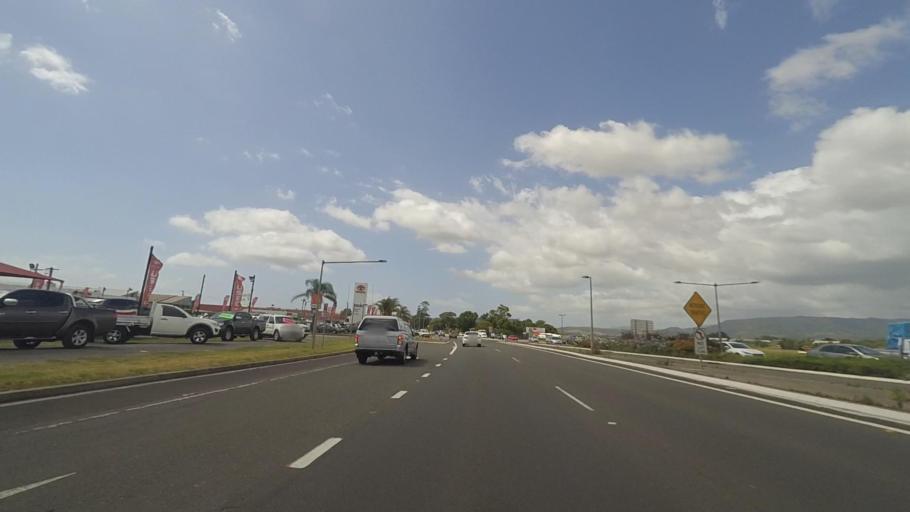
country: AU
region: New South Wales
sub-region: Shellharbour
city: Albion Park Rail
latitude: -34.5492
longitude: 150.7857
